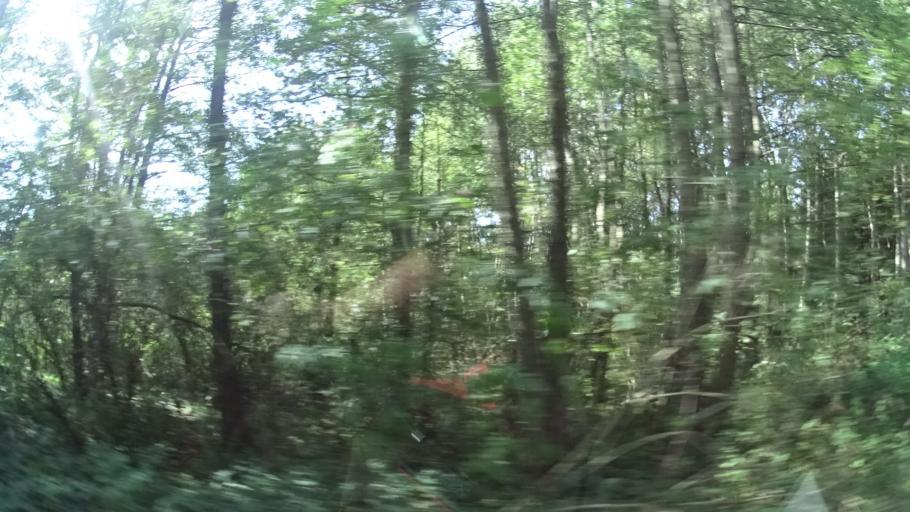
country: DE
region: Thuringia
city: Christes
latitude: 50.6452
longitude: 10.4652
